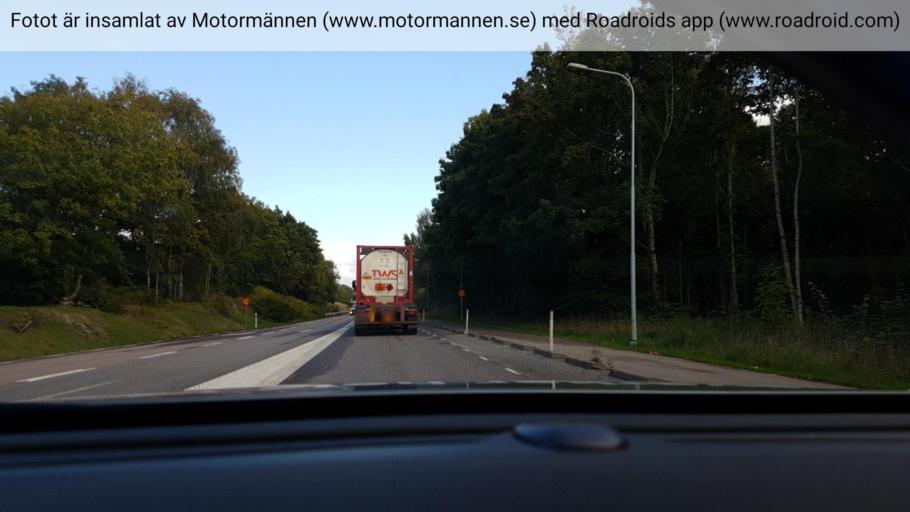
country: SE
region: Vaestra Goetaland
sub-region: Stenungsunds Kommun
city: Stenungsund
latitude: 58.0773
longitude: 11.8337
